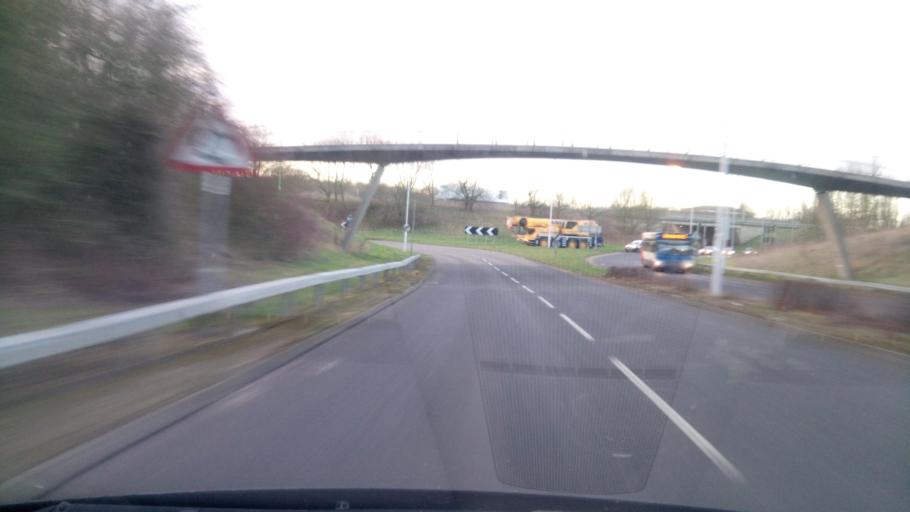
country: GB
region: England
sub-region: Peterborough
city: Marholm
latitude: 52.5732
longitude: -0.2961
